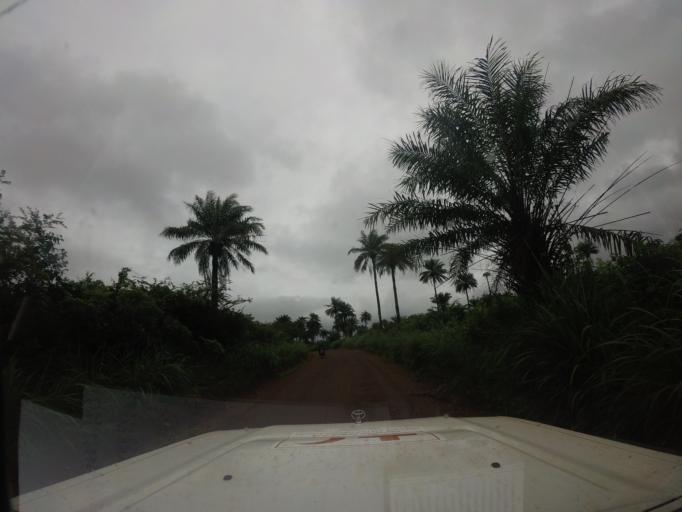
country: SL
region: Northern Province
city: Kambia
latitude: 9.1516
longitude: -12.8779
